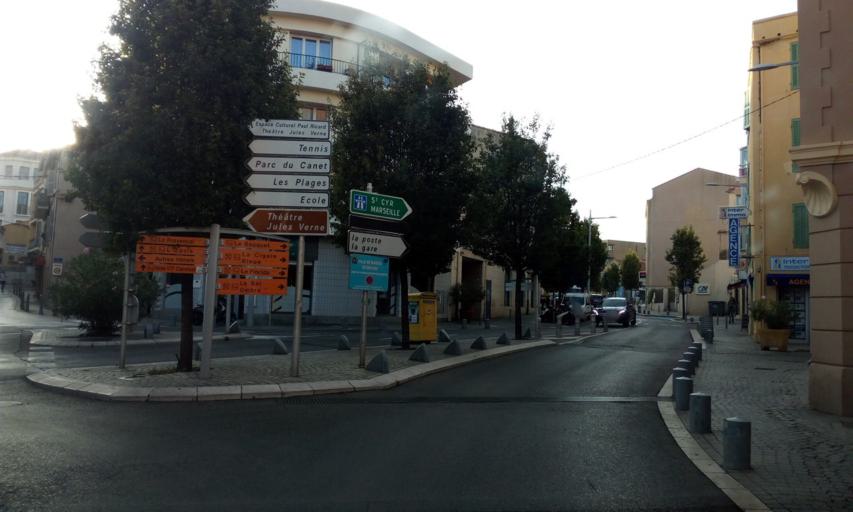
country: FR
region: Provence-Alpes-Cote d'Azur
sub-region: Departement du Var
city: Bandol
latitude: 43.1361
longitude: 5.7536
